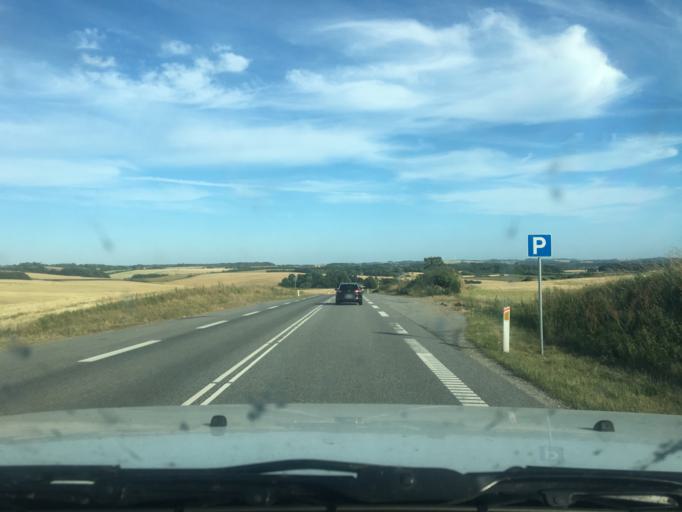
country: DK
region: Central Jutland
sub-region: Syddjurs Kommune
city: Hornslet
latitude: 56.3759
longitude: 10.3080
